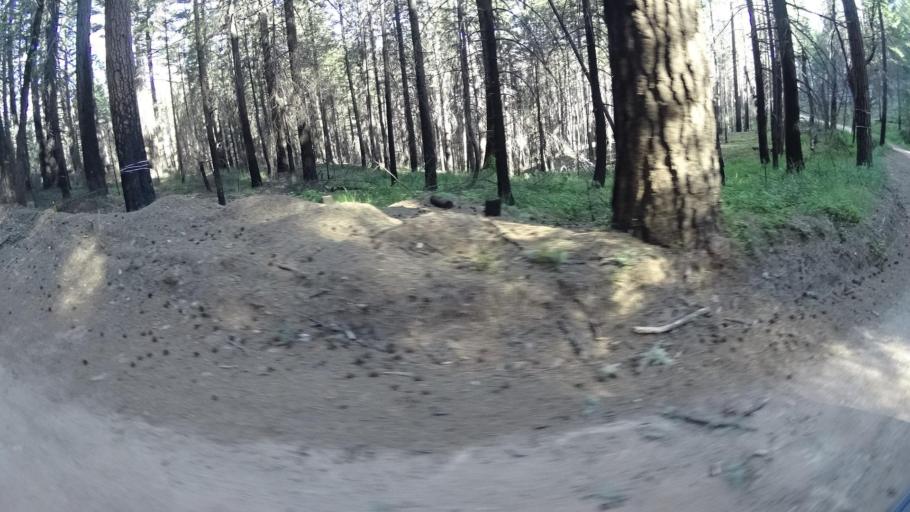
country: US
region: California
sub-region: Lake County
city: Upper Lake
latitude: 39.3636
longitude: -122.9917
